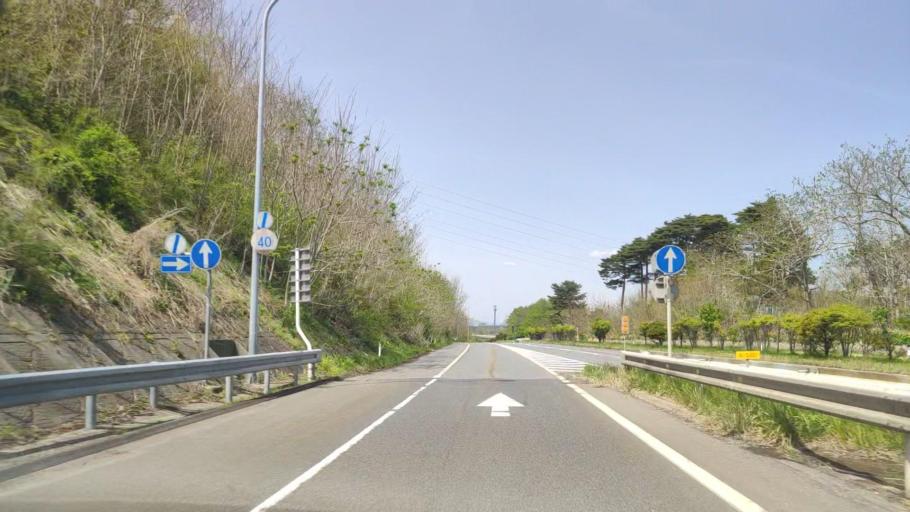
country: JP
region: Aomori
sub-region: Hachinohe Shi
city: Uchimaru
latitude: 40.4948
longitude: 141.4636
